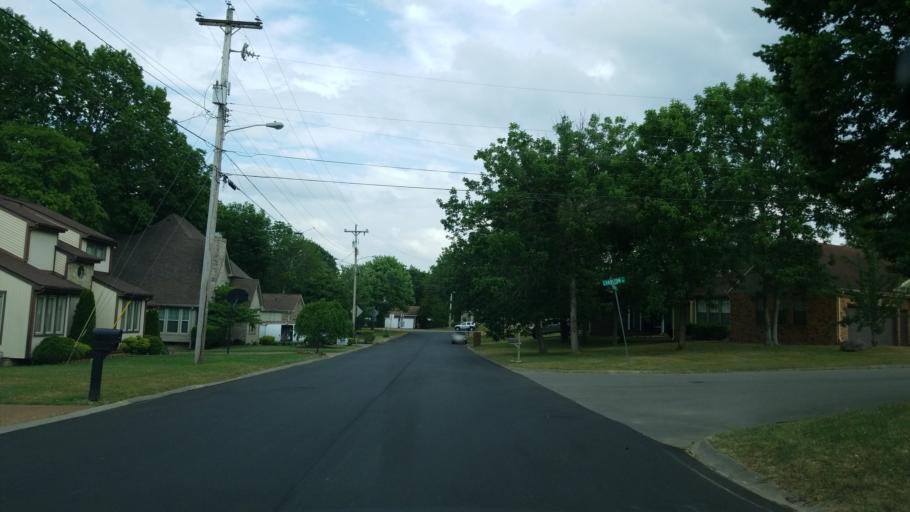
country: US
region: Tennessee
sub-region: Rutherford County
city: La Vergne
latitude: 36.0796
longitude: -86.6143
